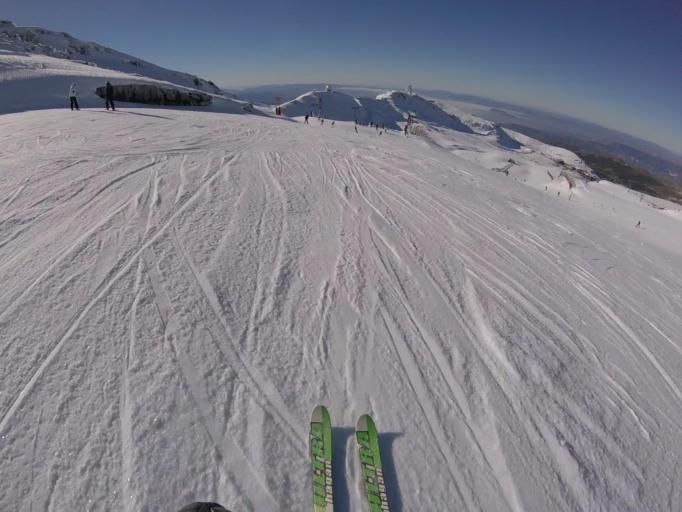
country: ES
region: Andalusia
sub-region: Provincia de Granada
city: Capileira
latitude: 37.0624
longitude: -3.3792
